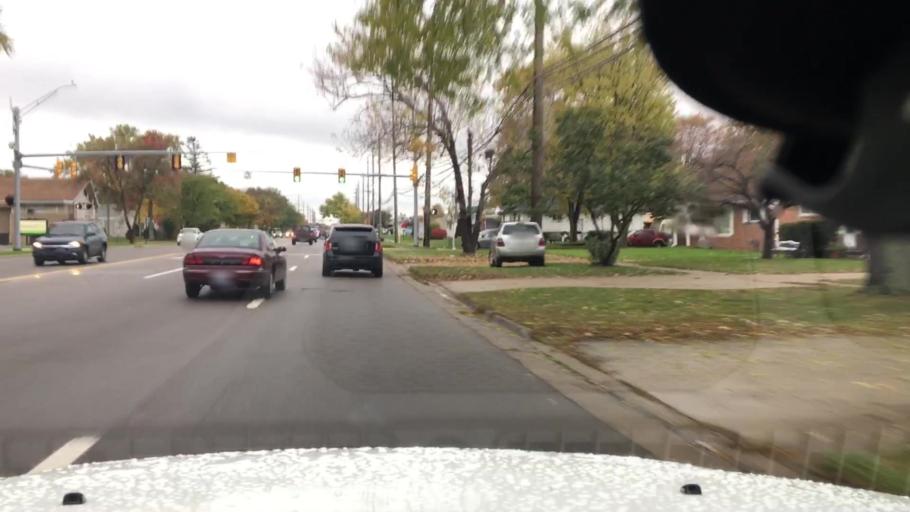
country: US
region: Michigan
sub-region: Oakland County
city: Madison Heights
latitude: 42.5051
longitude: -83.0949
